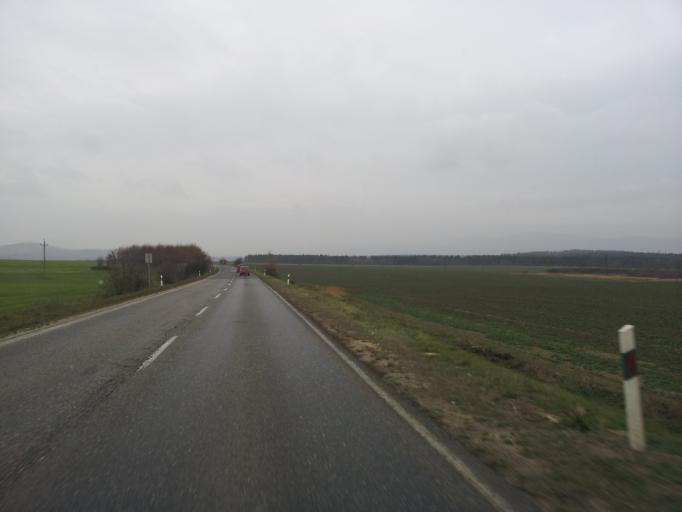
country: HU
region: Veszprem
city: Veszprem
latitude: 47.0816
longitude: 17.8903
